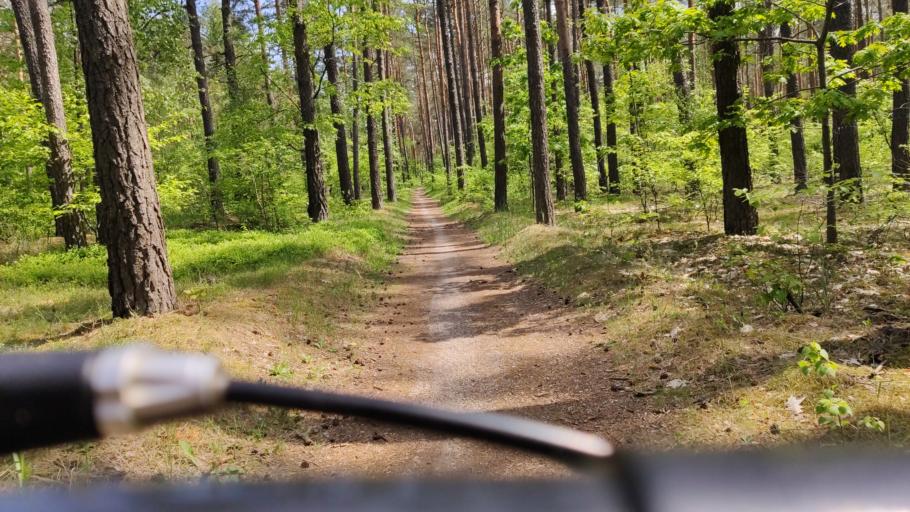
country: PL
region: Kujawsko-Pomorskie
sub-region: Wloclawek
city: Wloclawek
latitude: 52.6331
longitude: 19.1303
